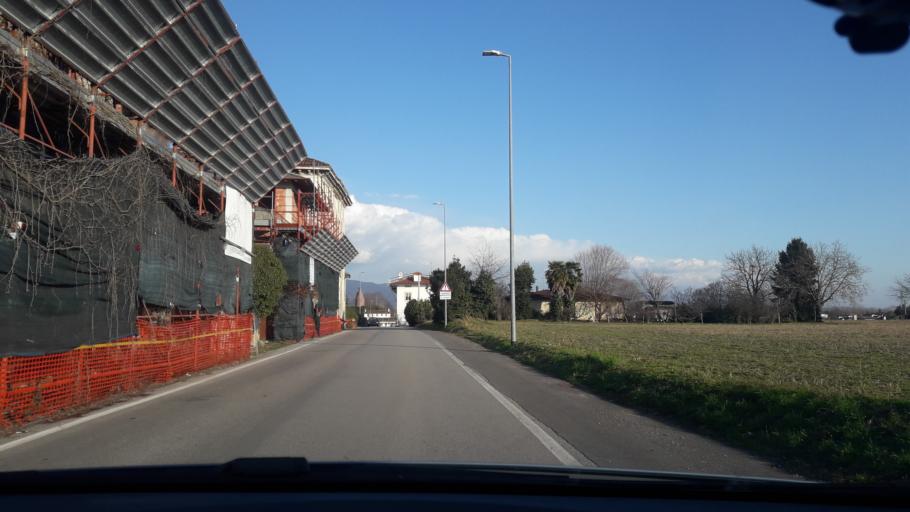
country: IT
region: Friuli Venezia Giulia
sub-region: Provincia di Udine
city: Reana del Rojale
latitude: 46.1442
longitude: 13.2383
